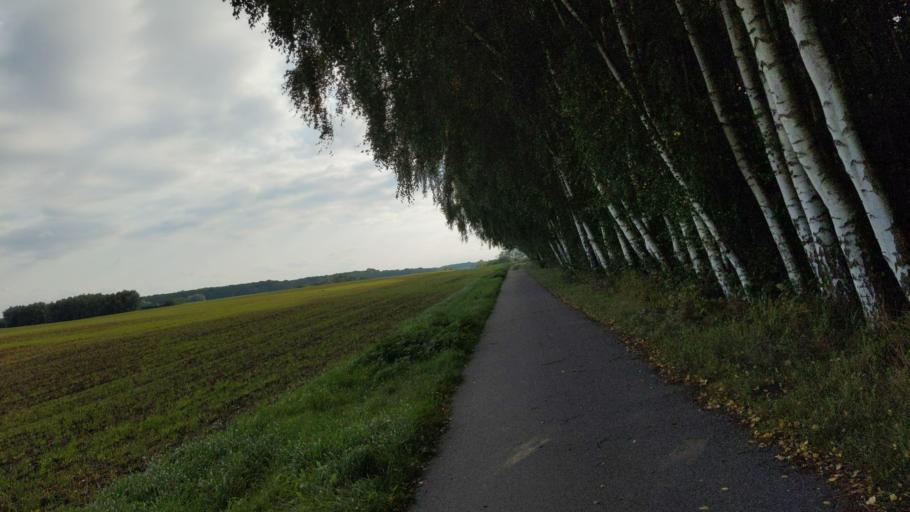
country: DE
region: Mecklenburg-Vorpommern
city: Dassow
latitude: 53.9763
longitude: 10.9624
